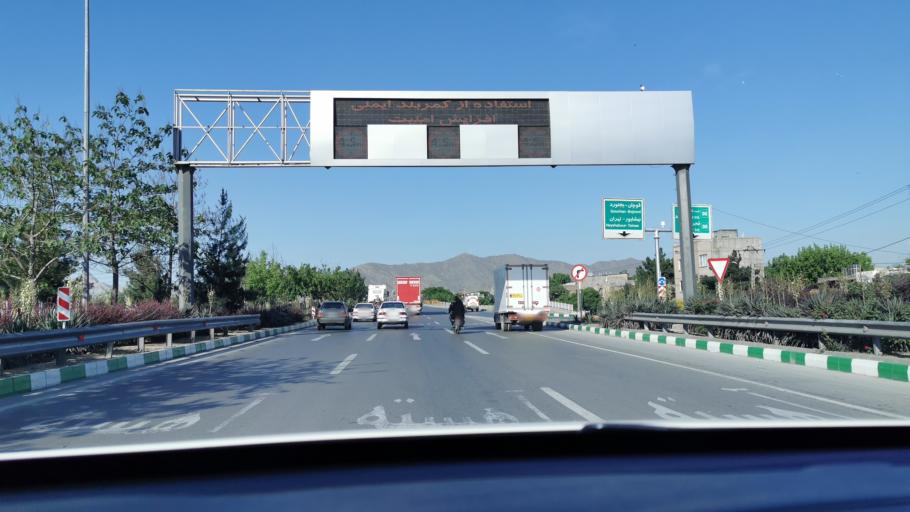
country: IR
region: Razavi Khorasan
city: Mashhad
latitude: 36.2552
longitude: 59.6186
